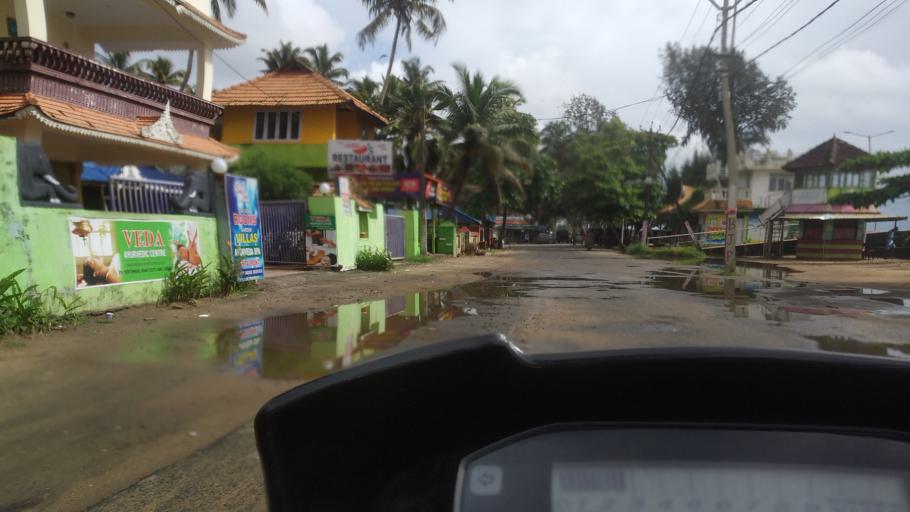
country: IN
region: Kerala
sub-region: Thrissur District
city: Kodungallur
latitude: 10.1399
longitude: 76.1792
